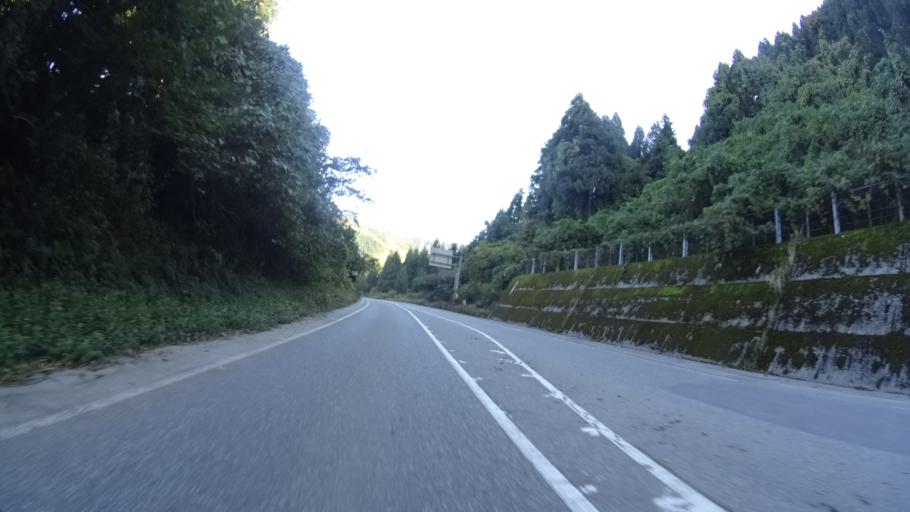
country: JP
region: Fukui
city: Maruoka
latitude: 36.1100
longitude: 136.3197
